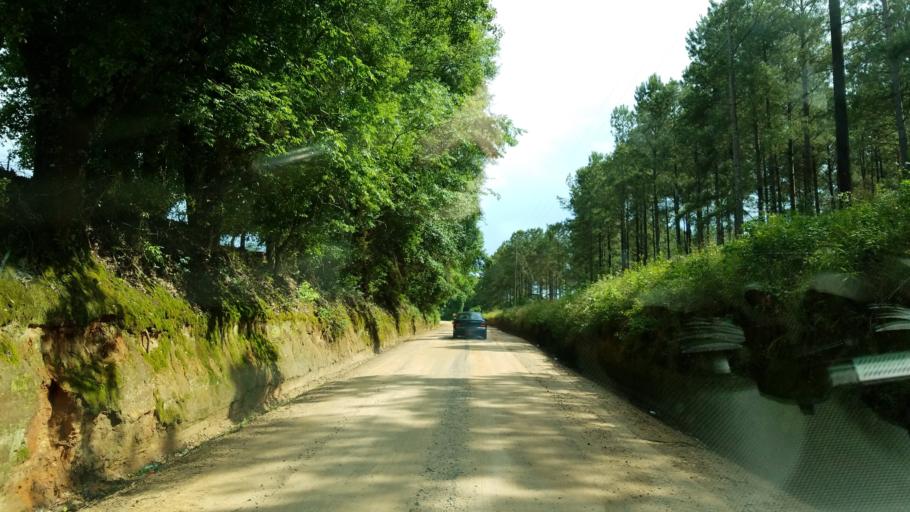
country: US
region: Georgia
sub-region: Houston County
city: Perry
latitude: 32.4420
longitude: -83.7890
